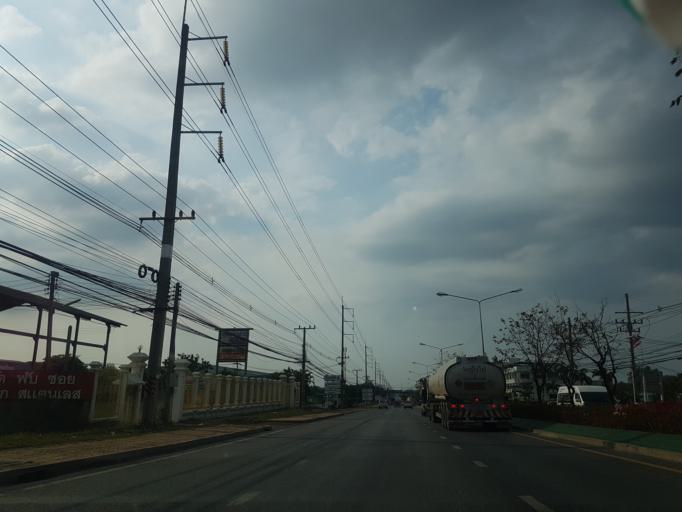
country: TH
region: Sara Buri
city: Phra Phutthabat
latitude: 14.7334
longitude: 100.7805
